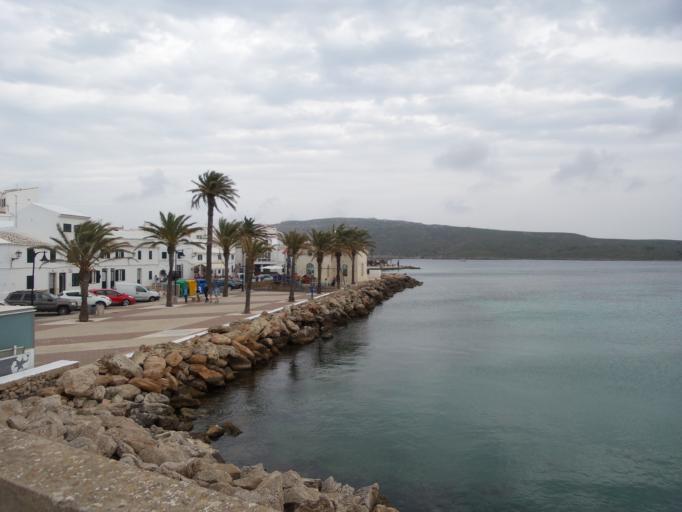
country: ES
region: Balearic Islands
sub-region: Illes Balears
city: Mercadal
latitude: 40.0552
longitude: 4.1314
